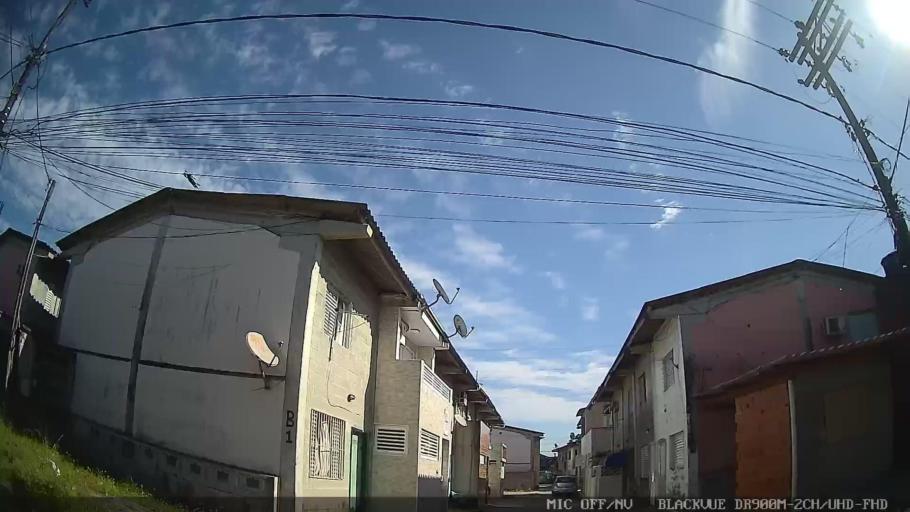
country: BR
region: Sao Paulo
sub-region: Guaruja
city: Guaruja
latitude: -23.9578
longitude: -46.2781
